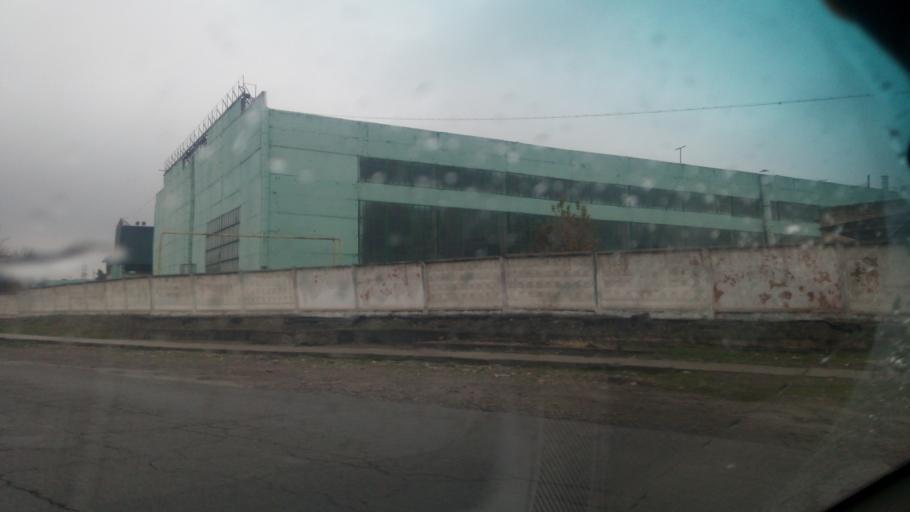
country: UZ
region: Toshkent Shahri
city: Bektemir
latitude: 41.2482
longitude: 69.3508
